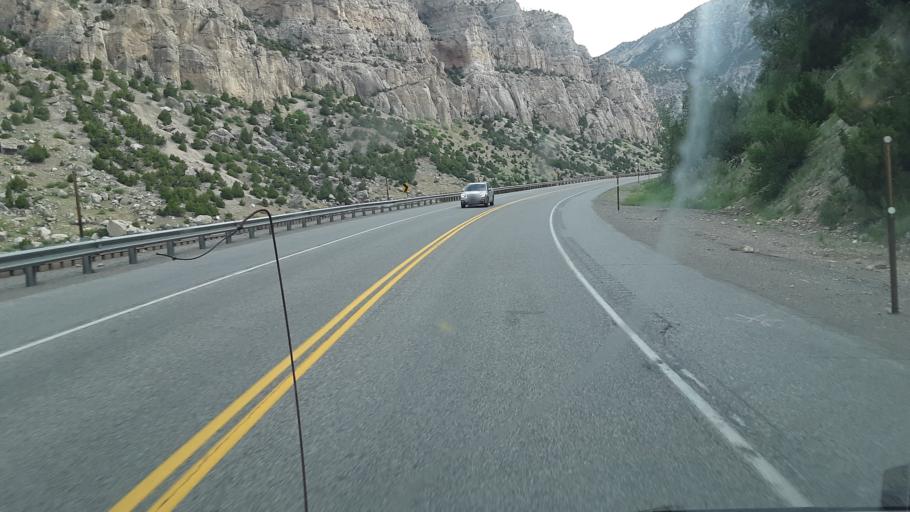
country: US
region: Wyoming
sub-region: Hot Springs County
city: Thermopolis
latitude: 43.5153
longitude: -108.1850
